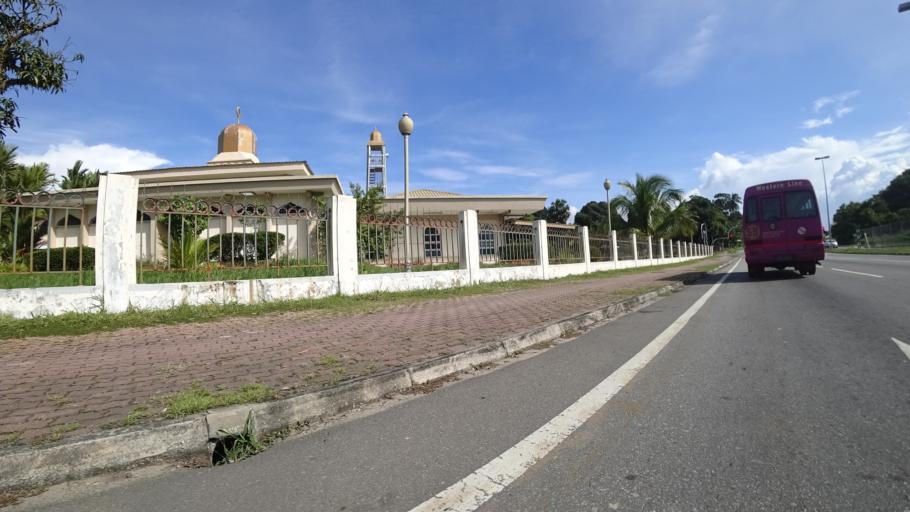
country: BN
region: Brunei and Muara
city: Bandar Seri Begawan
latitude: 4.9380
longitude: 114.8423
